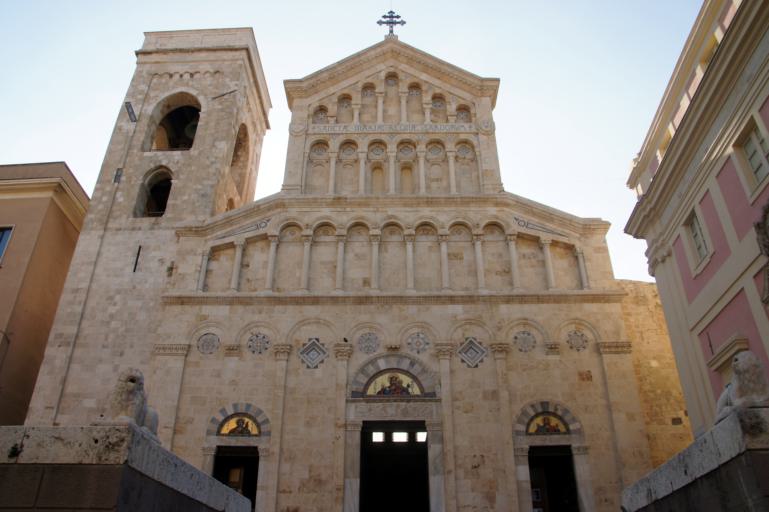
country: IT
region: Sardinia
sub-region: Provincia di Cagliari
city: Cagliari
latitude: 39.2184
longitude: 9.1167
